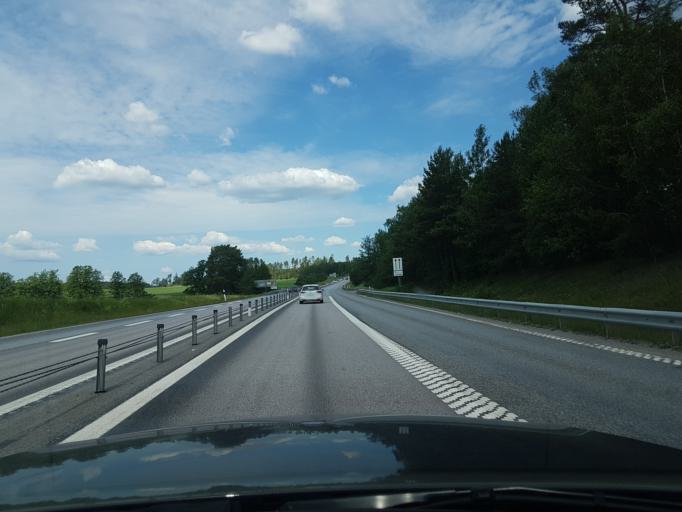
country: SE
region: Stockholm
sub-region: Osterakers Kommun
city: Akersberga
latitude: 59.5625
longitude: 18.2317
